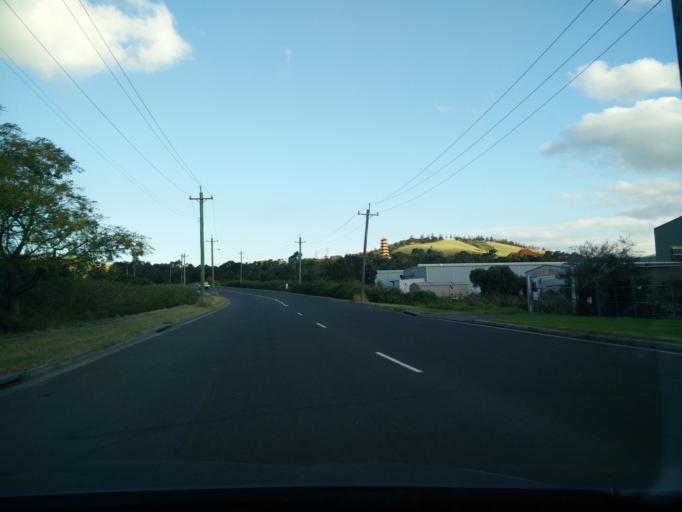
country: AU
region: New South Wales
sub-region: Wollongong
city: Cordeaux Heights
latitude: -34.4598
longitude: 150.8506
